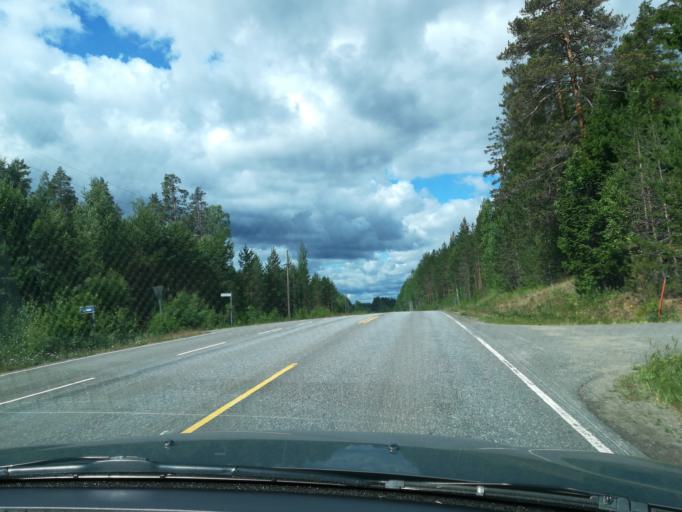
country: FI
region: Southern Savonia
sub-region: Mikkeli
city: Maentyharju
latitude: 61.3647
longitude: 26.9845
